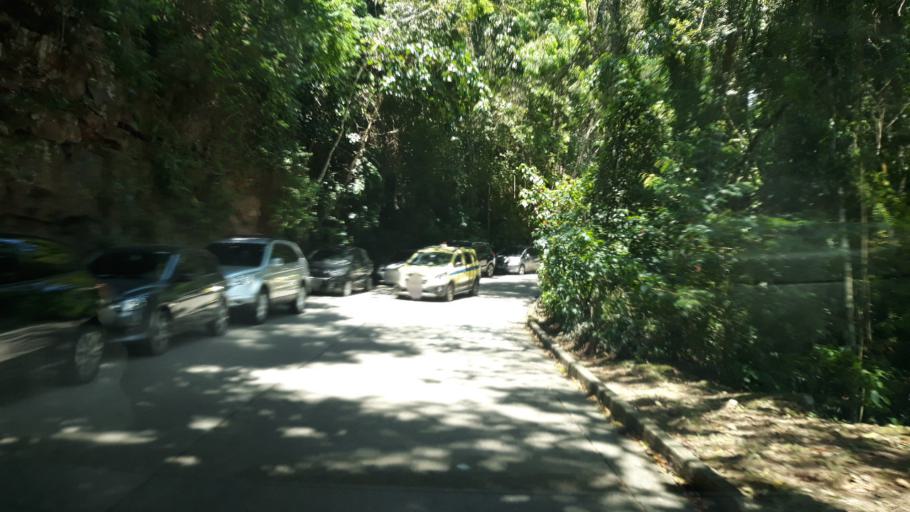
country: BR
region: Rio de Janeiro
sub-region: Rio De Janeiro
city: Rio de Janeiro
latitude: -22.9486
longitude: -43.2116
